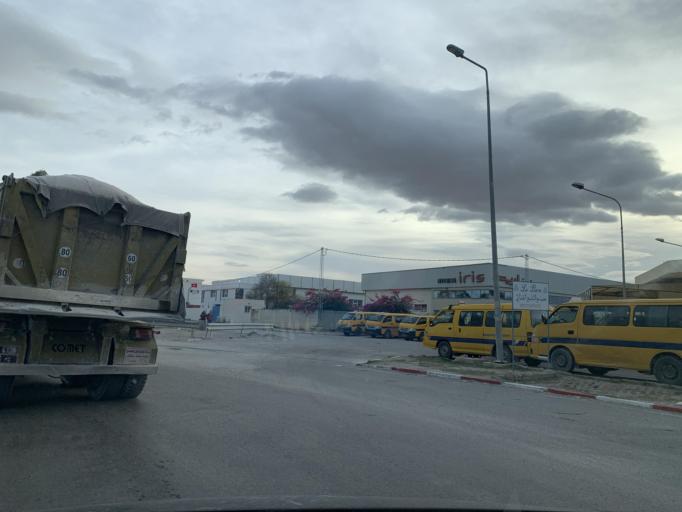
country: TN
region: Susah
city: Harqalah
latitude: 36.1108
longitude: 10.3858
